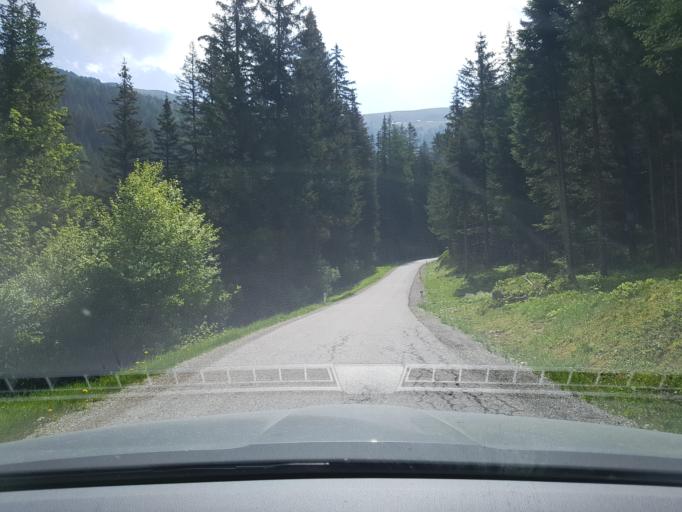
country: AT
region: Salzburg
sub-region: Politischer Bezirk Tamsweg
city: Thomatal
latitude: 47.0317
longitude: 13.7532
